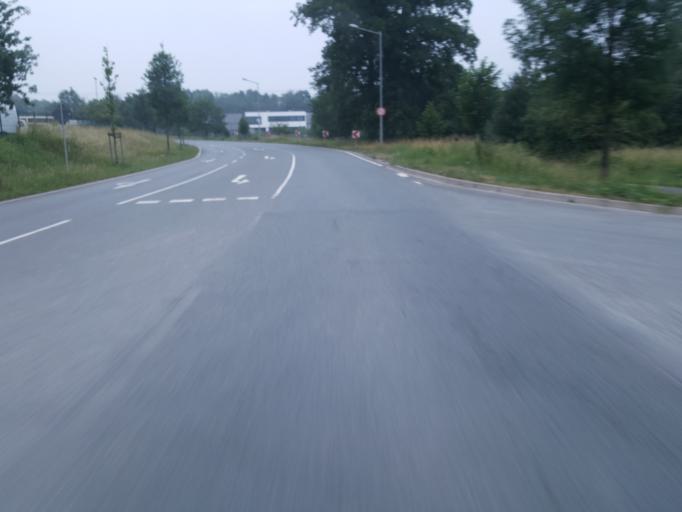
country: DE
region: North Rhine-Westphalia
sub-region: Regierungsbezirk Detmold
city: Kirchlengern
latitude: 52.1843
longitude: 8.6556
